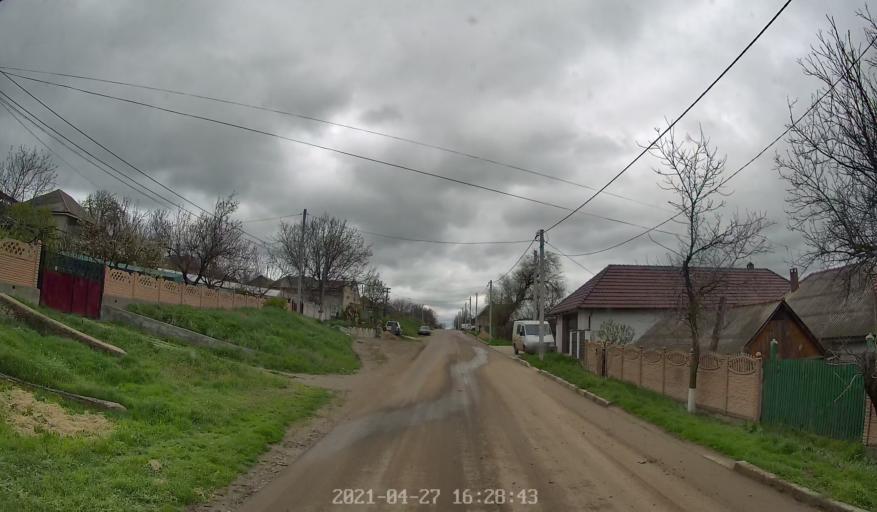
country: MD
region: Chisinau
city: Singera
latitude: 46.9707
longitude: 29.0444
